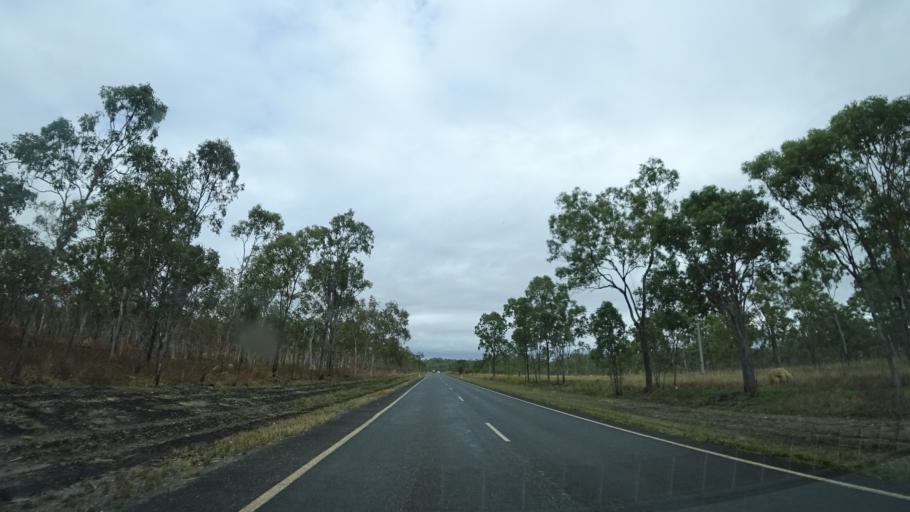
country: AU
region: Queensland
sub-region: Tablelands
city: Mareeba
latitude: -16.7678
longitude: 145.3409
